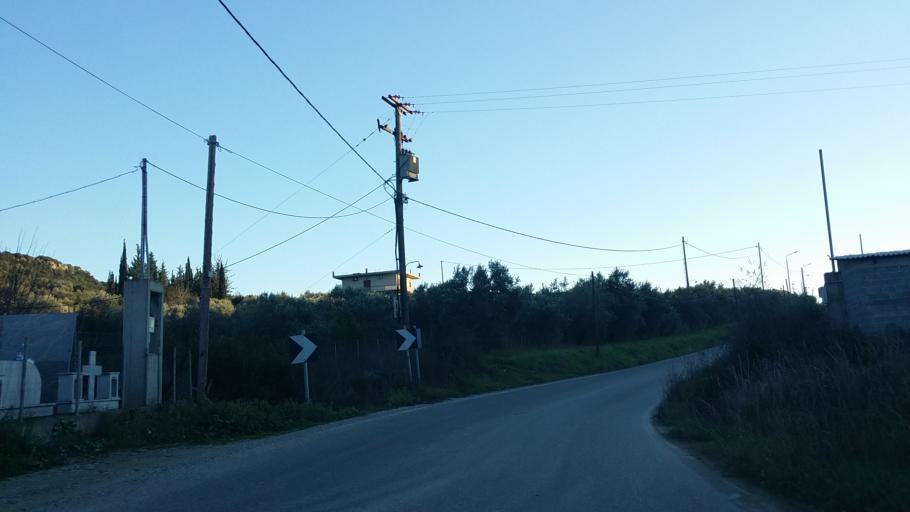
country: GR
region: West Greece
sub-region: Nomos Aitolias kai Akarnanias
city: Neapolis
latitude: 38.6968
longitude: 21.3536
